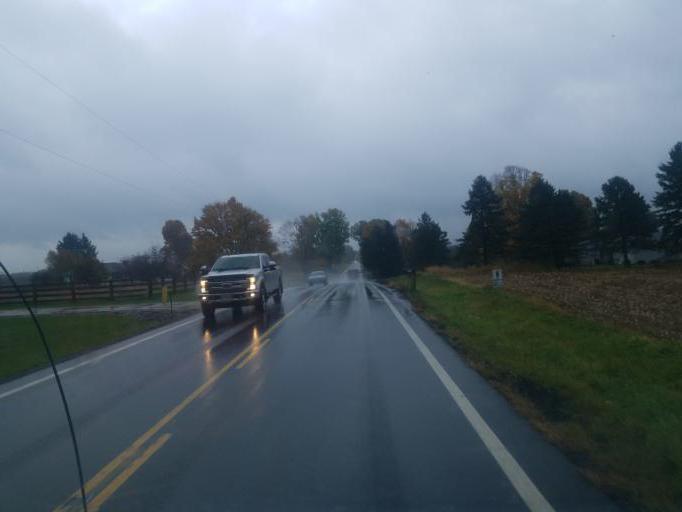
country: US
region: Ohio
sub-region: Knox County
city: Mount Vernon
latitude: 40.3581
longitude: -82.4502
